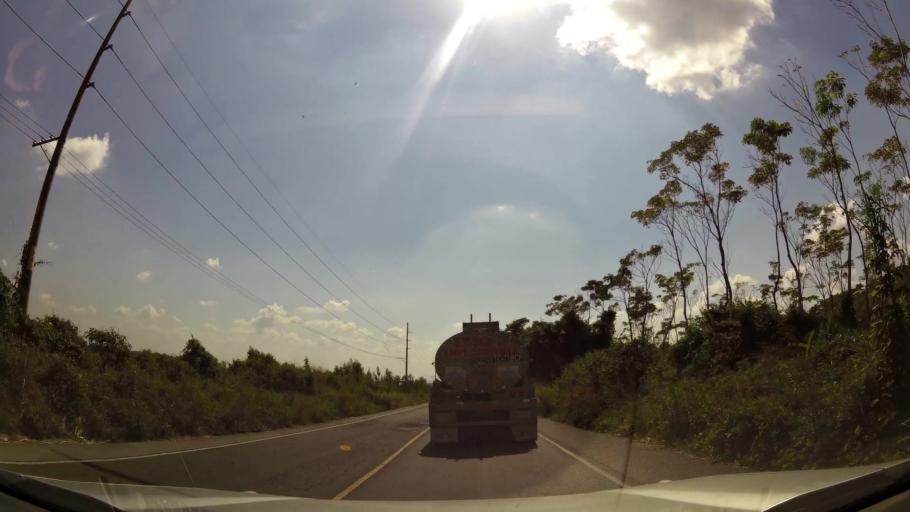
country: GT
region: Suchitepeque
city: Mazatenango
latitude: 14.5481
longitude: -91.5214
